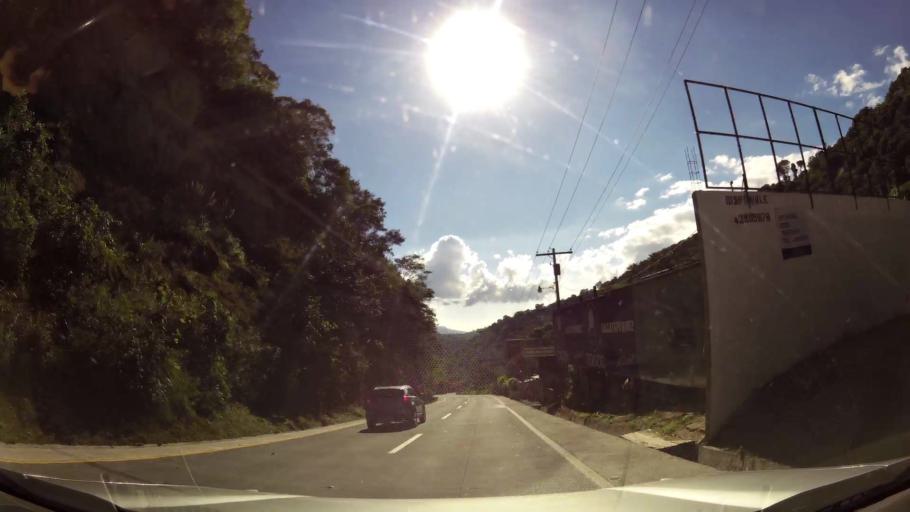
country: GT
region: Sacatepequez
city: Santa Lucia Milpas Altas
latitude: 14.5726
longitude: -90.6881
